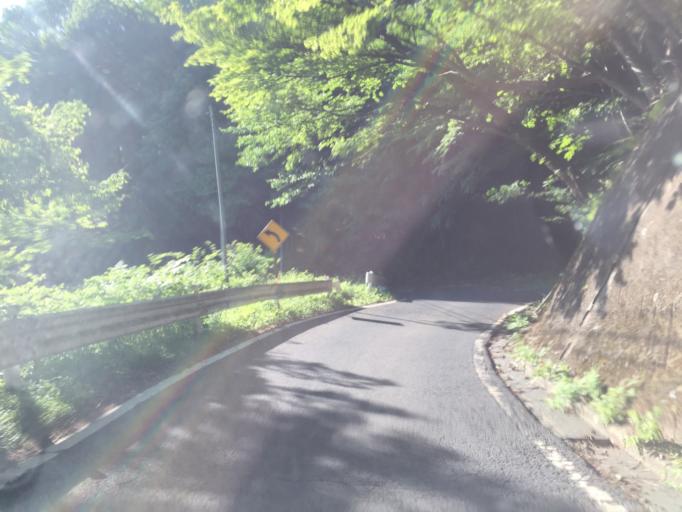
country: JP
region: Ibaraki
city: Kitaibaraki
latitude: 36.9038
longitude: 140.5919
